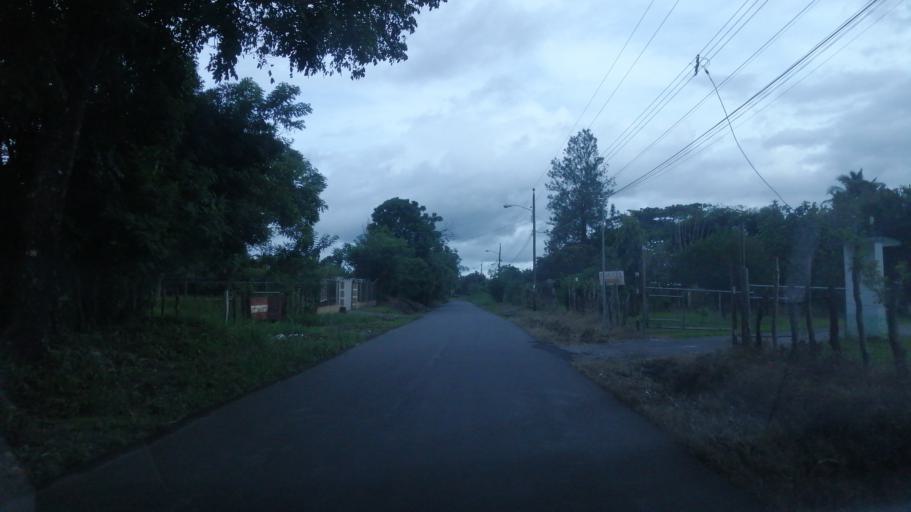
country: PA
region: Chiriqui
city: Tijera
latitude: 8.4519
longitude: -82.5255
